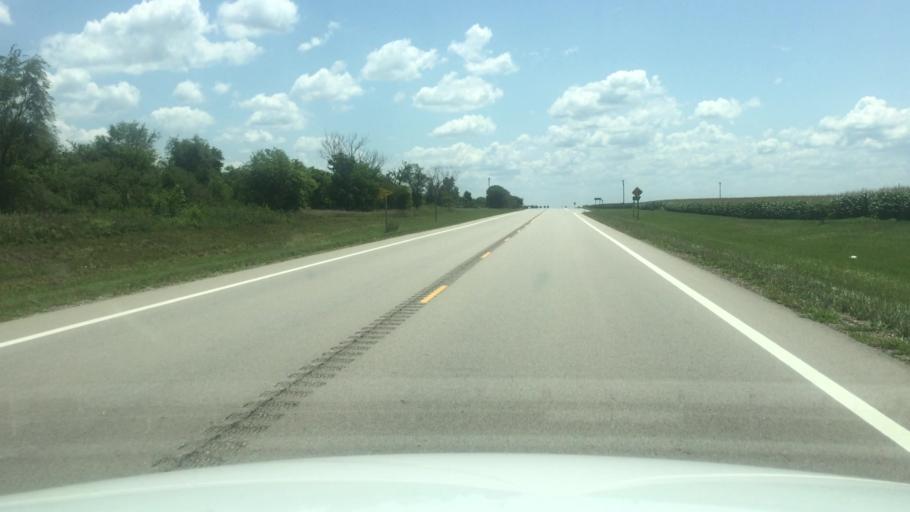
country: US
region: Kansas
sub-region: Brown County
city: Horton
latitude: 39.6410
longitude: -95.3543
